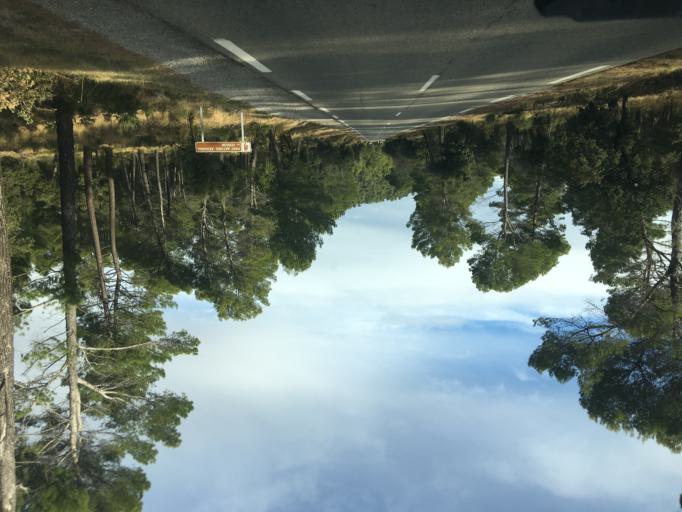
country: FR
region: Provence-Alpes-Cote d'Azur
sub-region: Departement du Var
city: Villecroze
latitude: 43.5908
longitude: 6.2576
